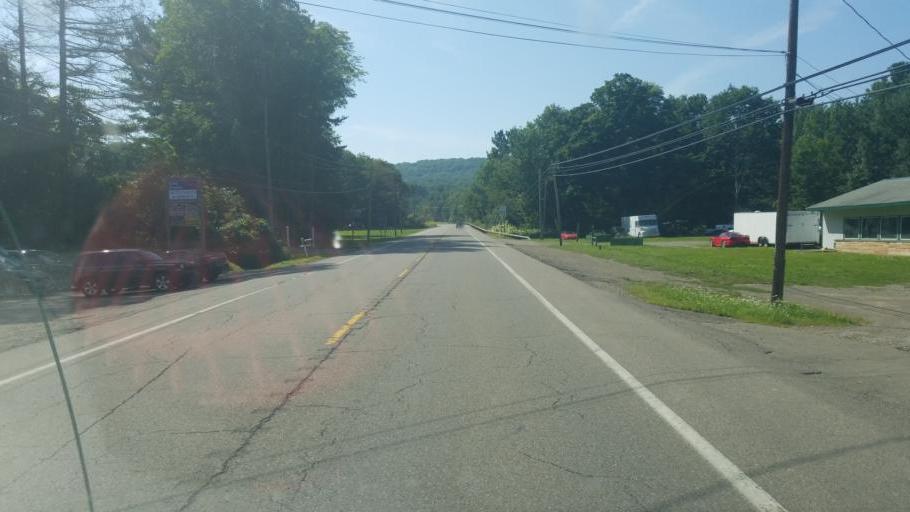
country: US
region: New York
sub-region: Allegany County
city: Wellsville
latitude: 42.1243
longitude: -77.9847
